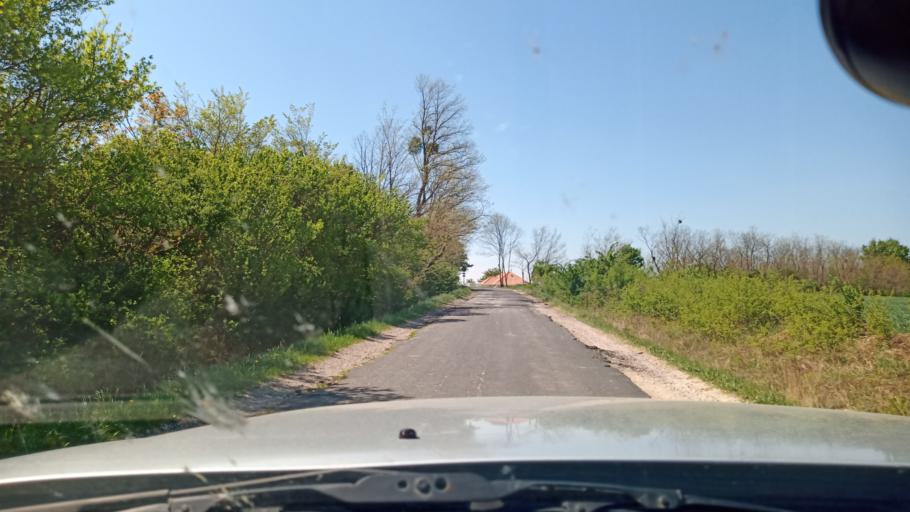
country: HU
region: Zala
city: Heviz
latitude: 46.7668
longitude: 17.1499
